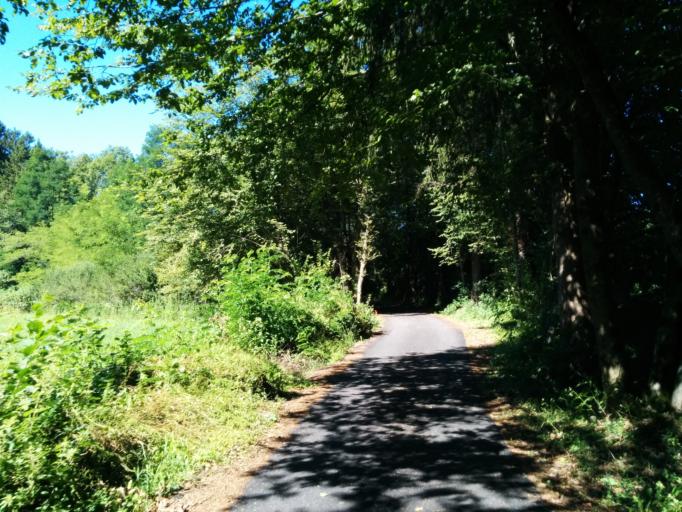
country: IT
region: Friuli Venezia Giulia
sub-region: Provincia di Udine
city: Villa Santina
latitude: 46.4060
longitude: 12.9263
